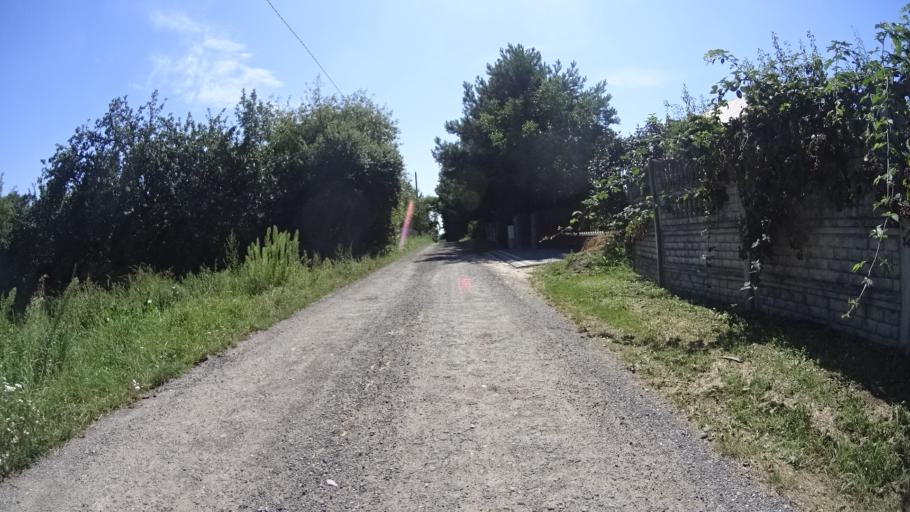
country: PL
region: Masovian Voivodeship
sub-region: Powiat bialobrzeski
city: Bialobrzegi
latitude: 51.6692
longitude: 20.8844
